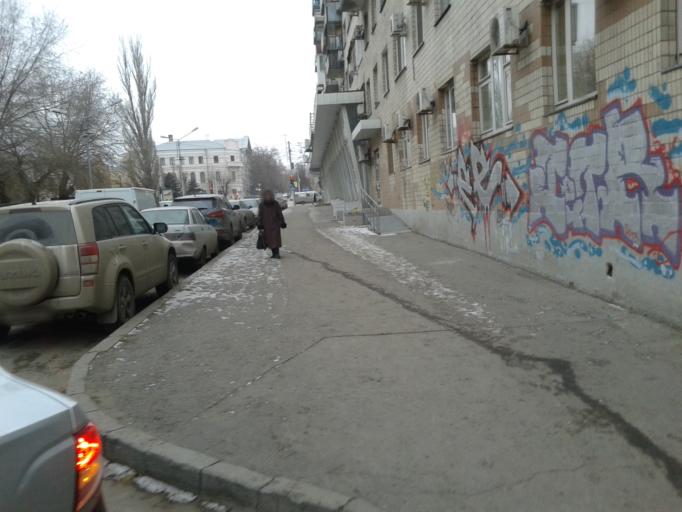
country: RU
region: Volgograd
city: Volgograd
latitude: 48.7041
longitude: 44.5149
